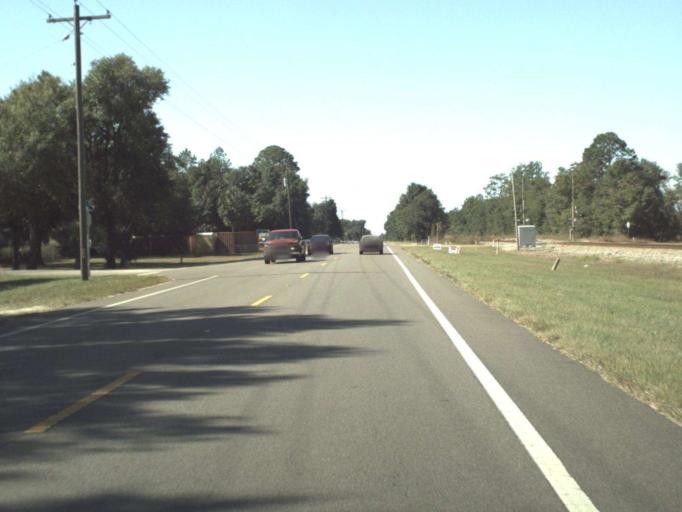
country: US
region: Florida
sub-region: Okaloosa County
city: Crestview
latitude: 30.7053
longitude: -86.7755
